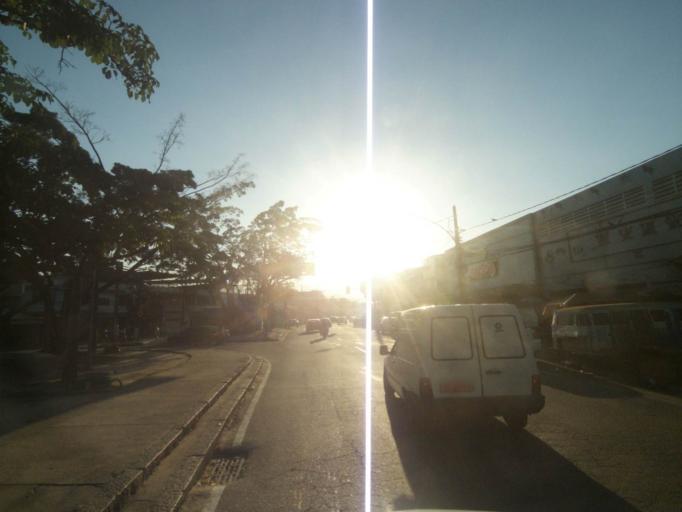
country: BR
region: Rio de Janeiro
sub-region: Sao Joao De Meriti
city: Sao Joao de Meriti
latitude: -22.9471
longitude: -43.3604
